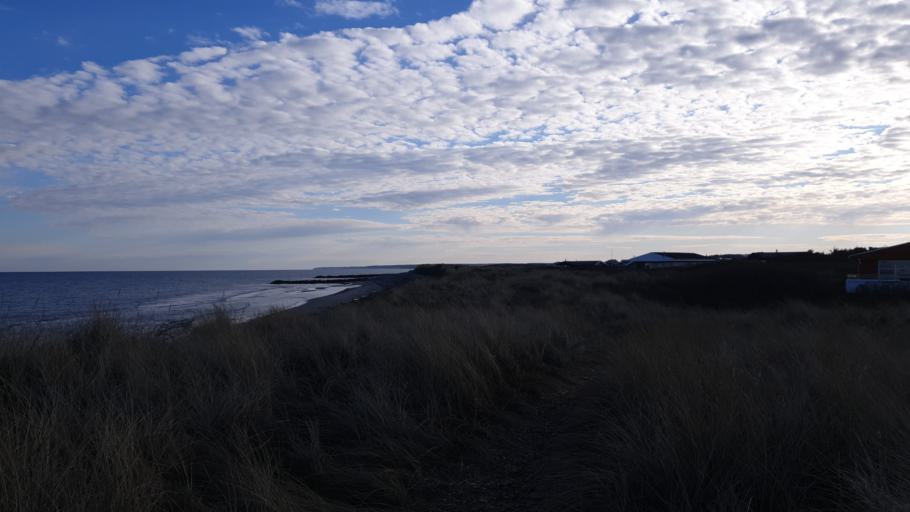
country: DK
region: North Denmark
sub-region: Hjorring Kommune
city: Hjorring
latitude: 57.4889
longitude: 9.8193
